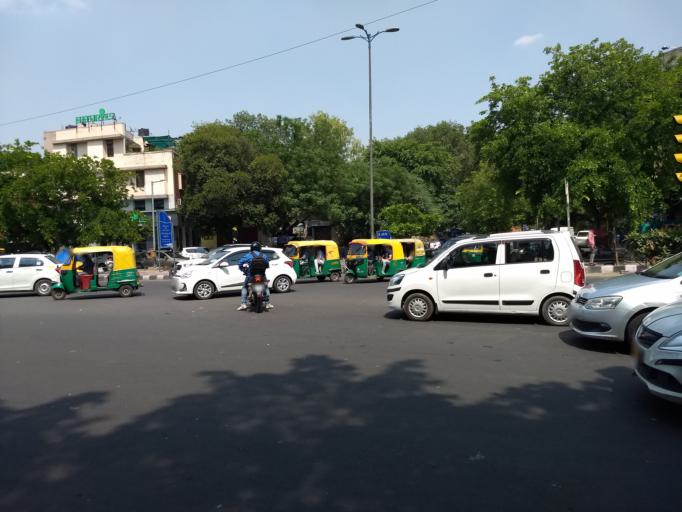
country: IN
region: NCT
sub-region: New Delhi
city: New Delhi
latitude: 28.5508
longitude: 77.2040
